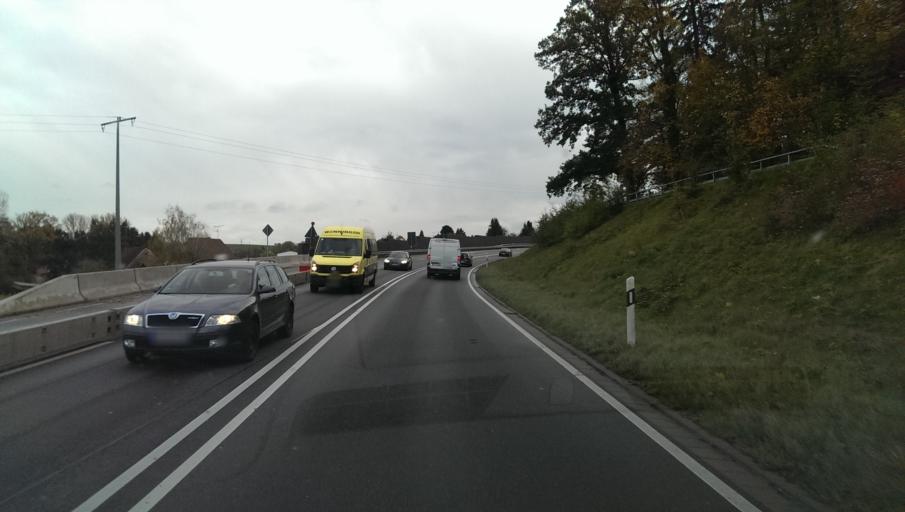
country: DE
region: Baden-Wuerttemberg
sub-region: Karlsruhe Region
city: Aglasterhausen
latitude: 49.3322
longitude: 8.9740
